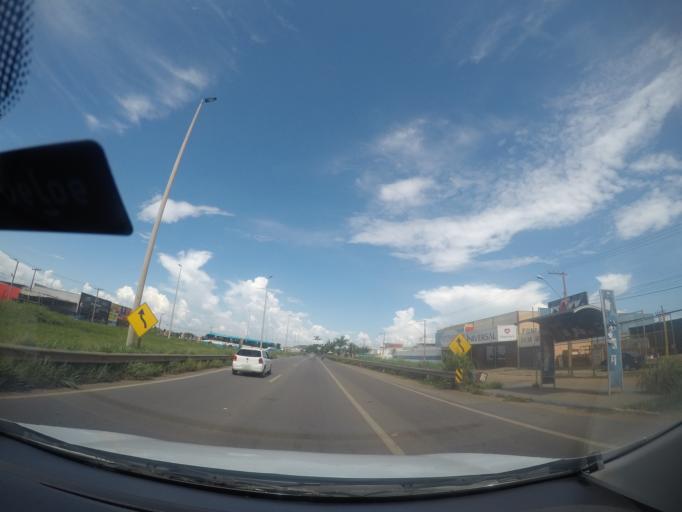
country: BR
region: Goias
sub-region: Trindade
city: Trindade
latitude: -16.6568
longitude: -49.3806
